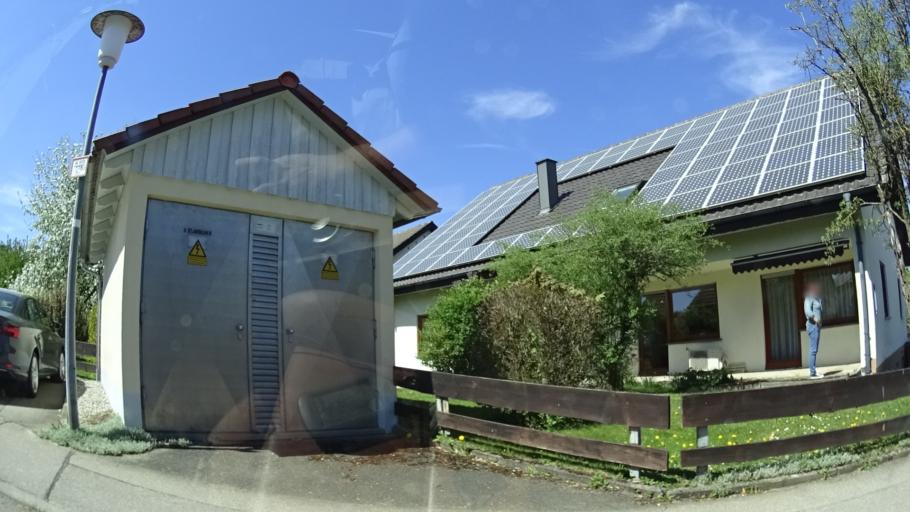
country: DE
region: Baden-Wuerttemberg
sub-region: Freiburg Region
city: Zimmern ob Rottweil
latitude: 48.1654
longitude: 8.5910
